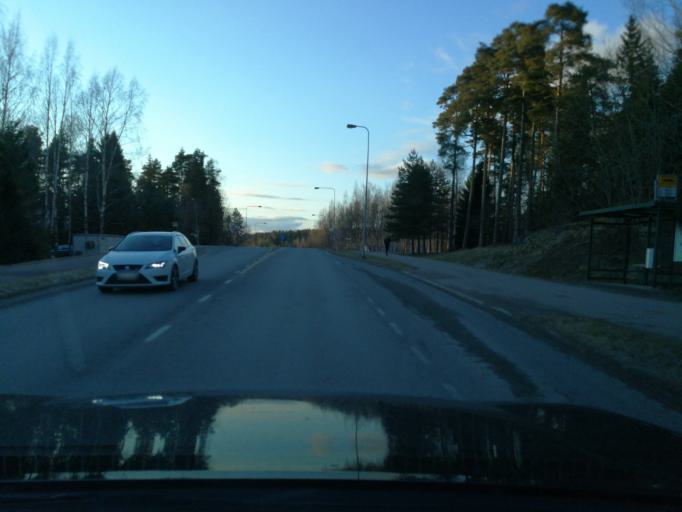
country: FI
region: Varsinais-Suomi
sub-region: Turku
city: Kaarina
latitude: 60.4108
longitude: 22.3137
